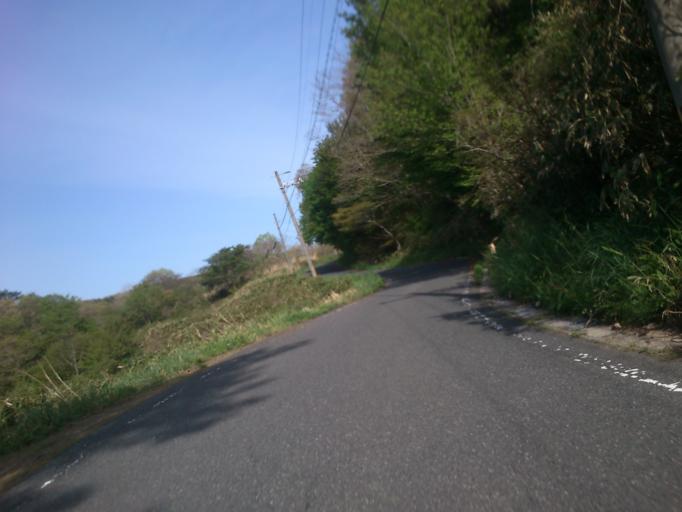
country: JP
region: Kyoto
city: Miyazu
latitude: 35.6454
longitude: 135.1831
